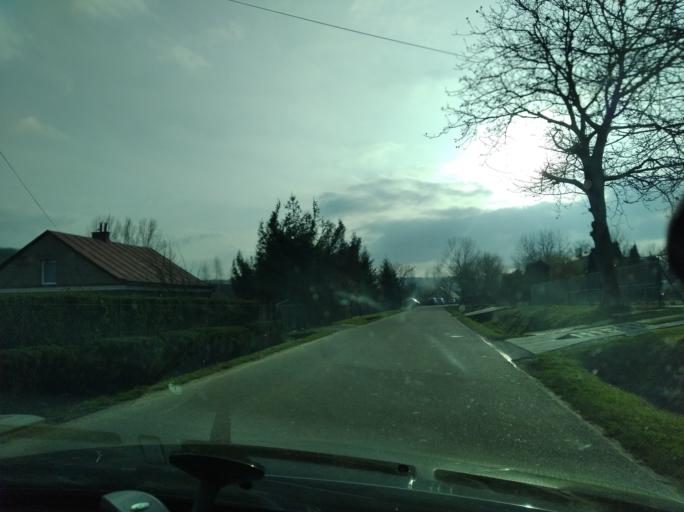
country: PL
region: Subcarpathian Voivodeship
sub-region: Powiat przeworski
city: Lopuszka Wielka
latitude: 49.9489
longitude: 22.4090
